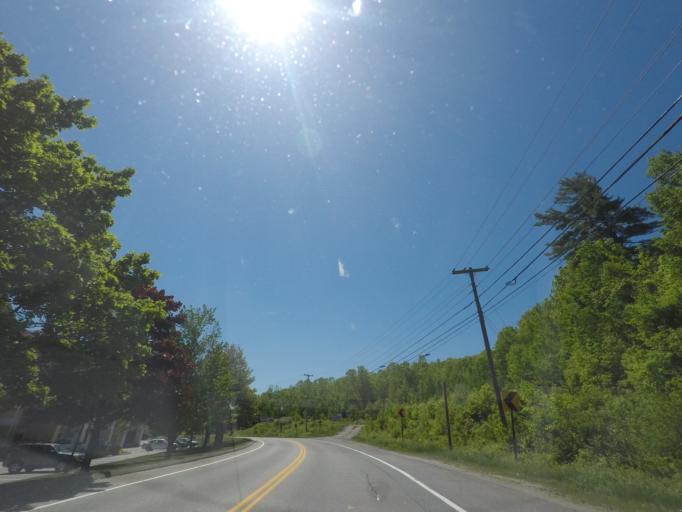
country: US
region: Maine
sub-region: Kennebec County
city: Augusta
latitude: 44.3122
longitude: -69.8133
